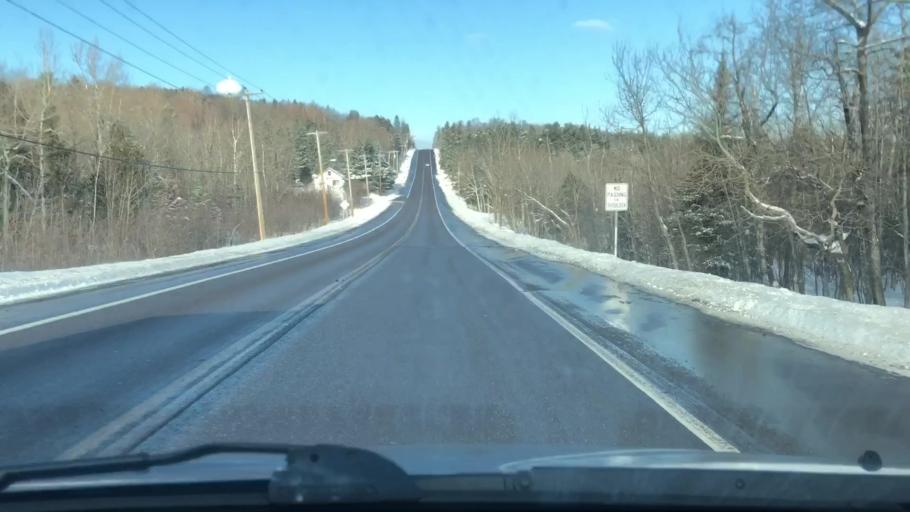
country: US
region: Minnesota
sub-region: Saint Louis County
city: Duluth
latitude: 46.8077
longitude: -92.1321
